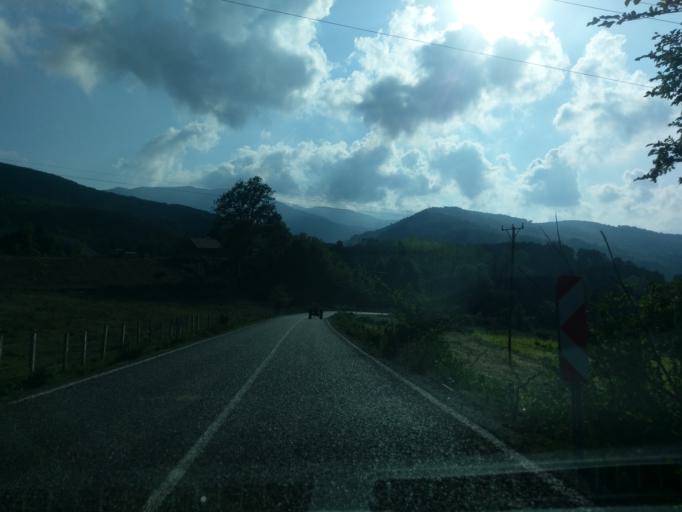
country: TR
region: Sinop
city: Ayancik
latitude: 41.8892
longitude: 34.4946
